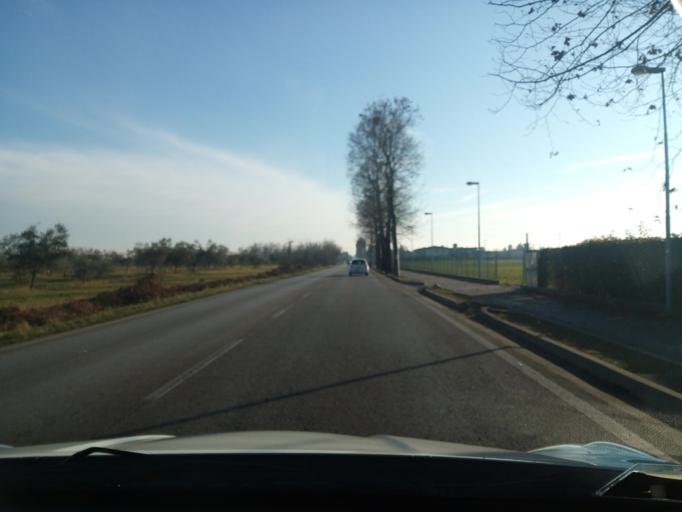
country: IT
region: Veneto
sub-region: Provincia di Vicenza
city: Thiene
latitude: 45.6807
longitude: 11.4856
